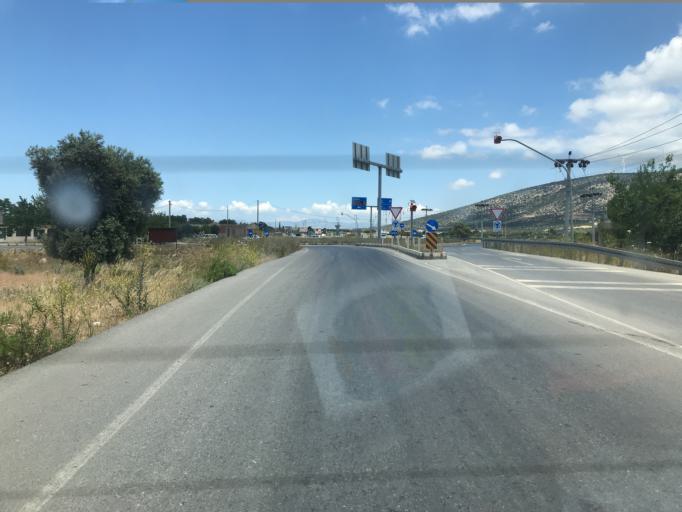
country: TR
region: Aydin
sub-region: Didim
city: Didim
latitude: 37.4229
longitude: 27.3708
